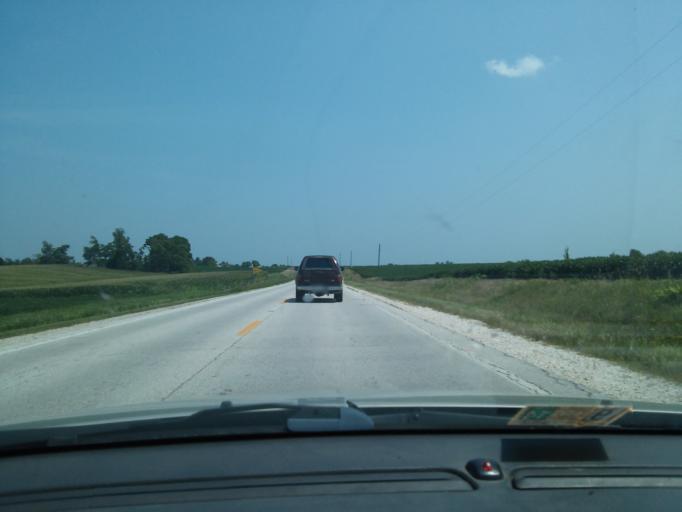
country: US
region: Illinois
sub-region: Pike County
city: Pittsfield
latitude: 39.5784
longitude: -90.9067
